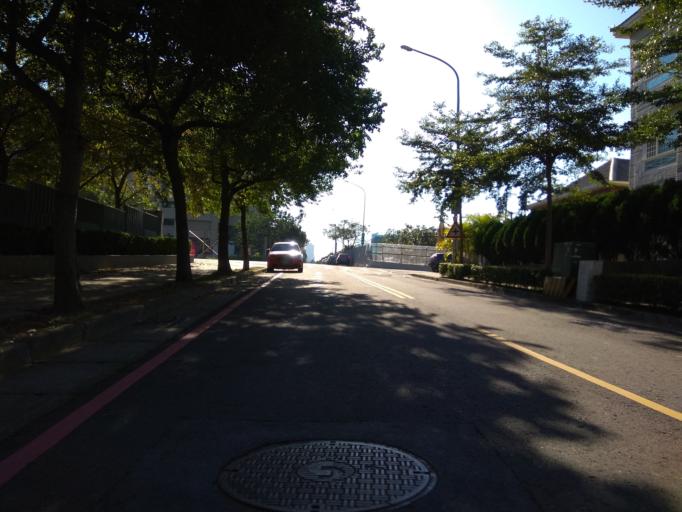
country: TW
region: Taiwan
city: Taoyuan City
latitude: 25.0218
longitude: 121.2198
